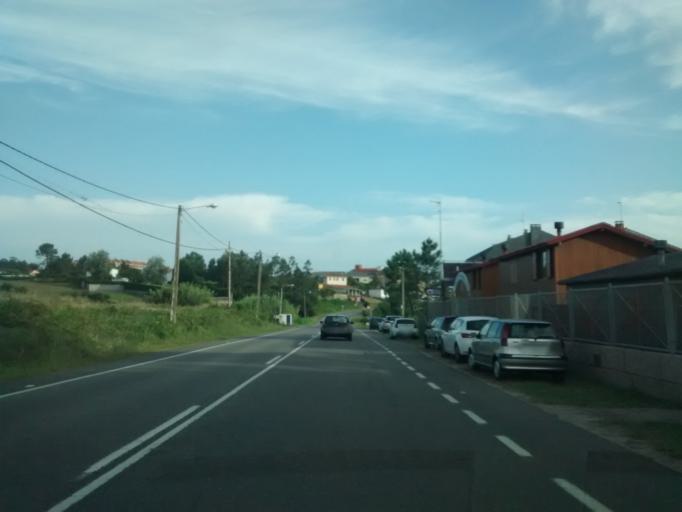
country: ES
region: Galicia
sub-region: Provincia de Pontevedra
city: Sanxenxo
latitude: 42.3961
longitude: -8.8445
